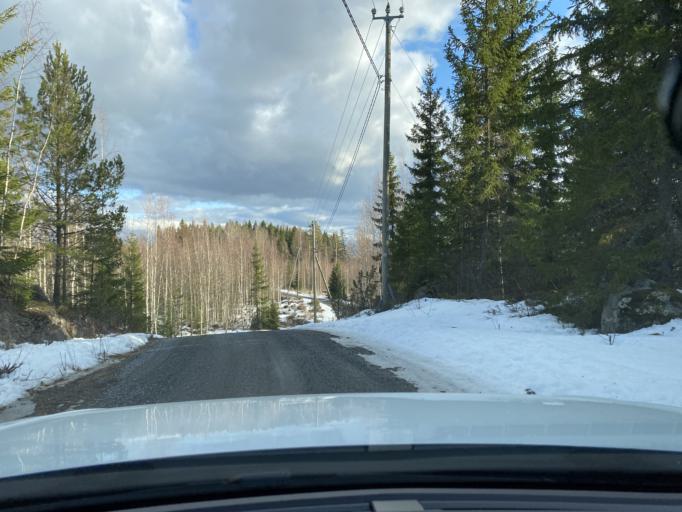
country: FI
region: Pirkanmaa
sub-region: Lounais-Pirkanmaa
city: Mouhijaervi
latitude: 61.4438
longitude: 22.9611
